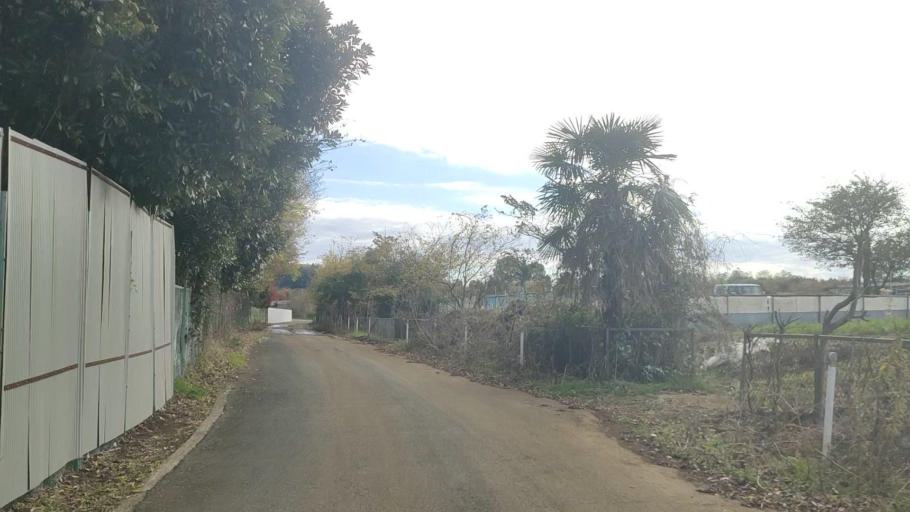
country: JP
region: Kanagawa
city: Minami-rinkan
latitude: 35.4889
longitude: 139.4927
